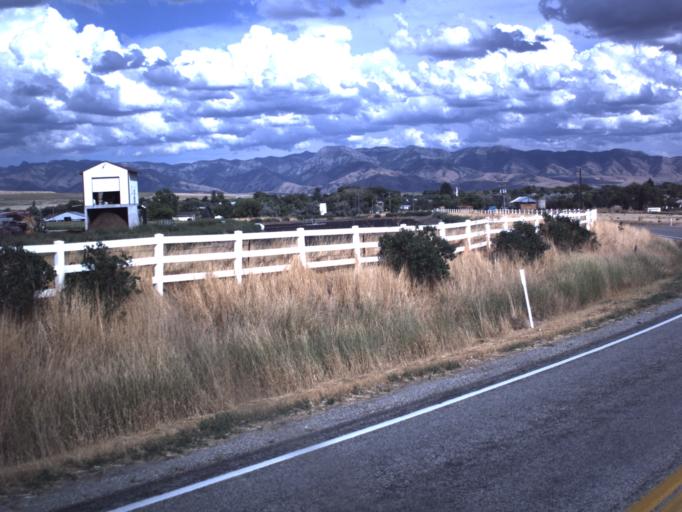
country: US
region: Utah
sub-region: Cache County
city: Benson
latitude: 41.8631
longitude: -112.0042
